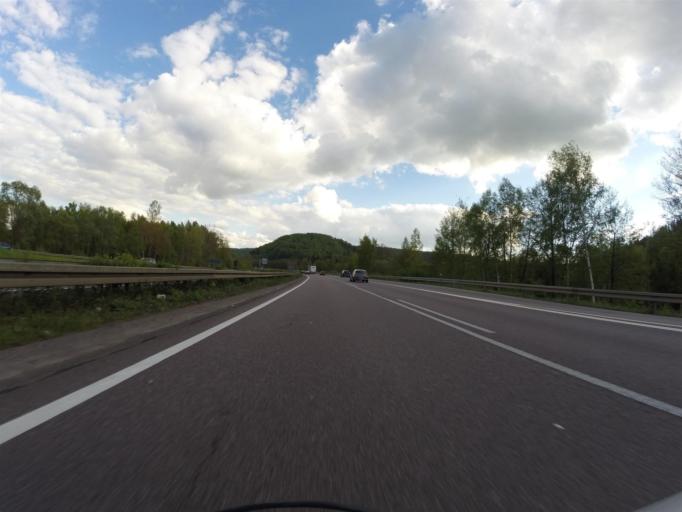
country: DE
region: Saarland
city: Rehlingen-Siersburg
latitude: 49.3629
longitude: 6.6944
